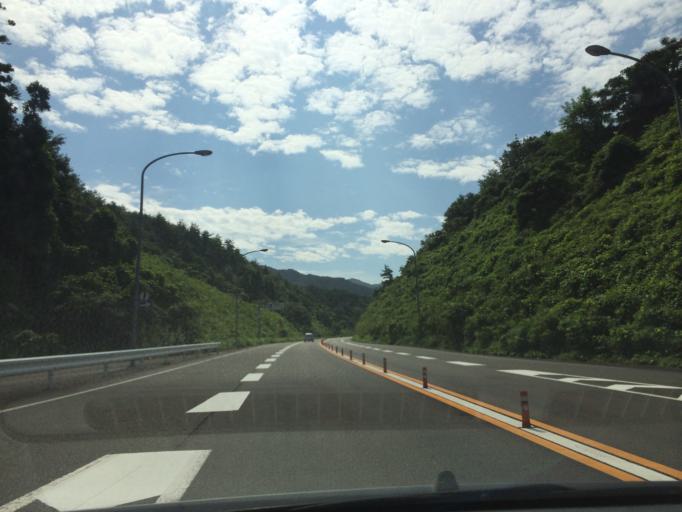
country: JP
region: Tottori
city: Kurayoshi
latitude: 35.3387
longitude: 133.7523
